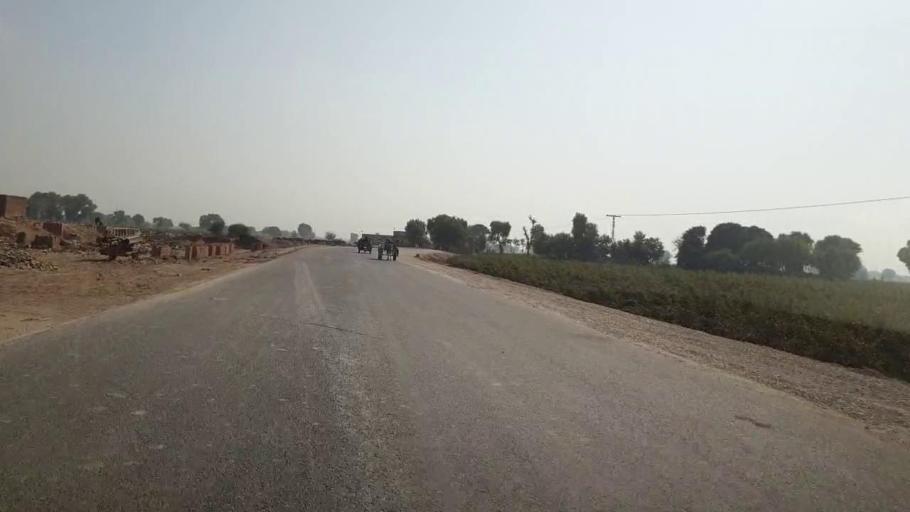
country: PK
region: Sindh
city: Dadu
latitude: 26.6770
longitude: 67.7765
